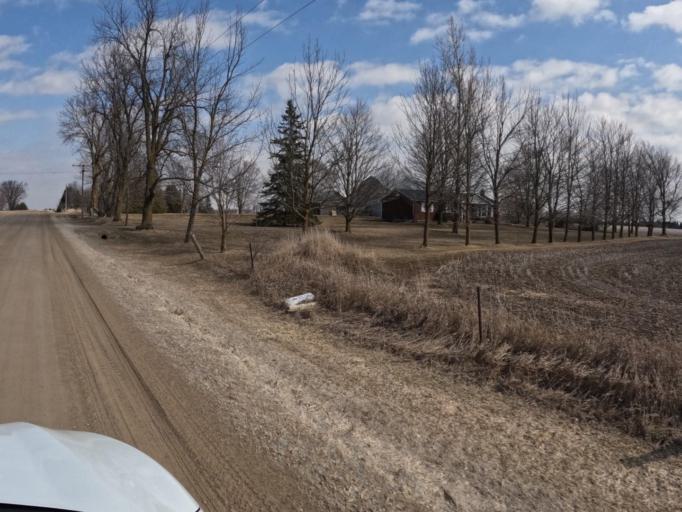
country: CA
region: Ontario
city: Orangeville
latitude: 43.9134
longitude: -80.2538
